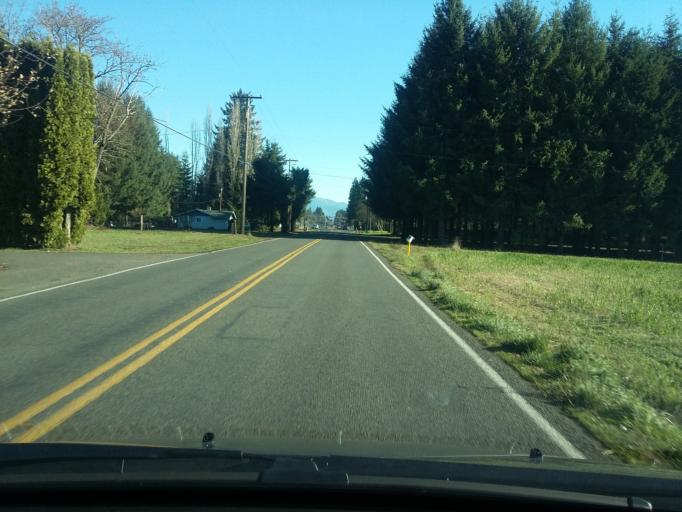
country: US
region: Washington
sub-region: Clark County
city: Five Corners
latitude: 45.7079
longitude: -122.5612
